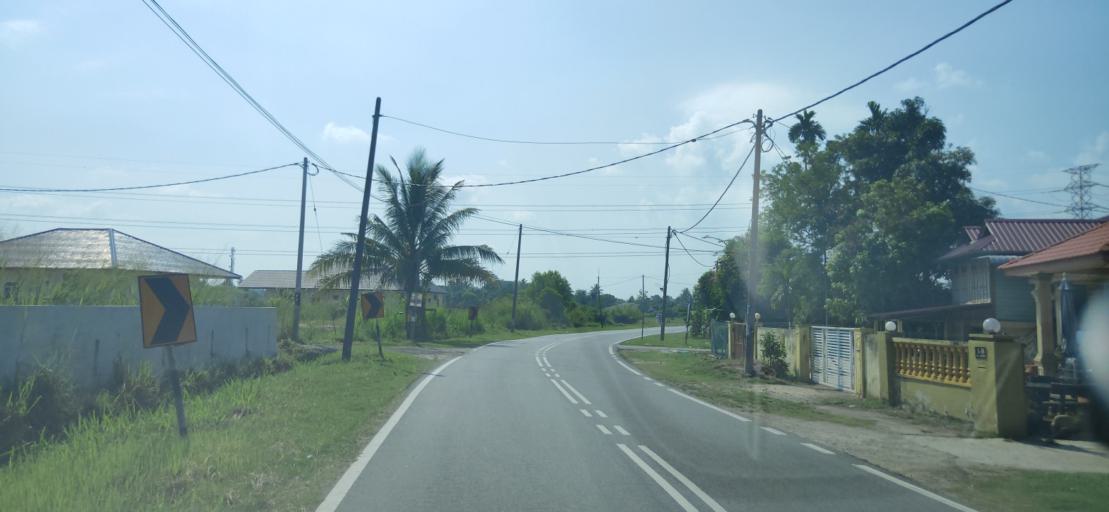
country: MY
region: Kedah
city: Sungai Petani
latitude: 5.6597
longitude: 100.4697
